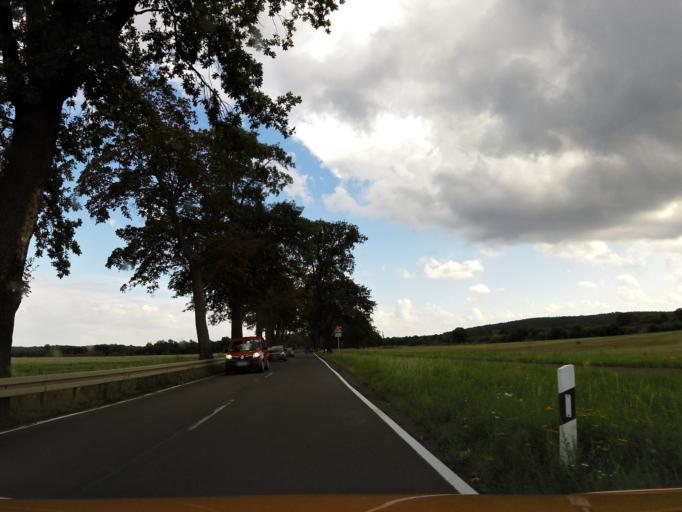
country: DE
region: Brandenburg
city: Potsdam
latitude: 52.4650
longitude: 13.0241
